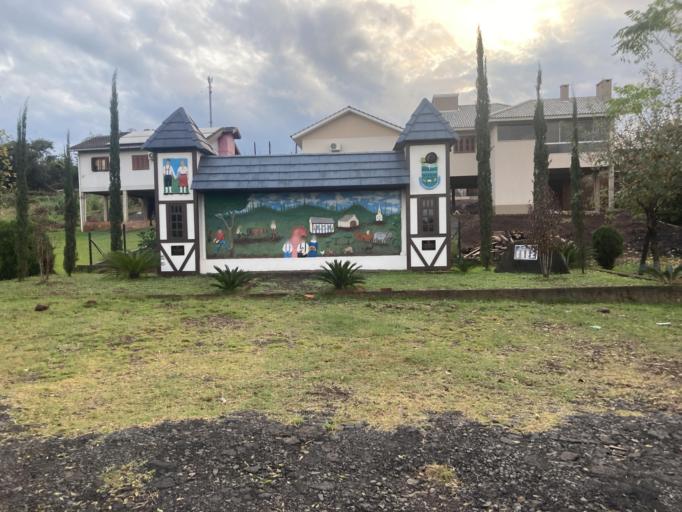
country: BR
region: Rio Grande do Sul
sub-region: Sao Pedro Do Butia
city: Butia Inferior
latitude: -27.9929
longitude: -54.8337
